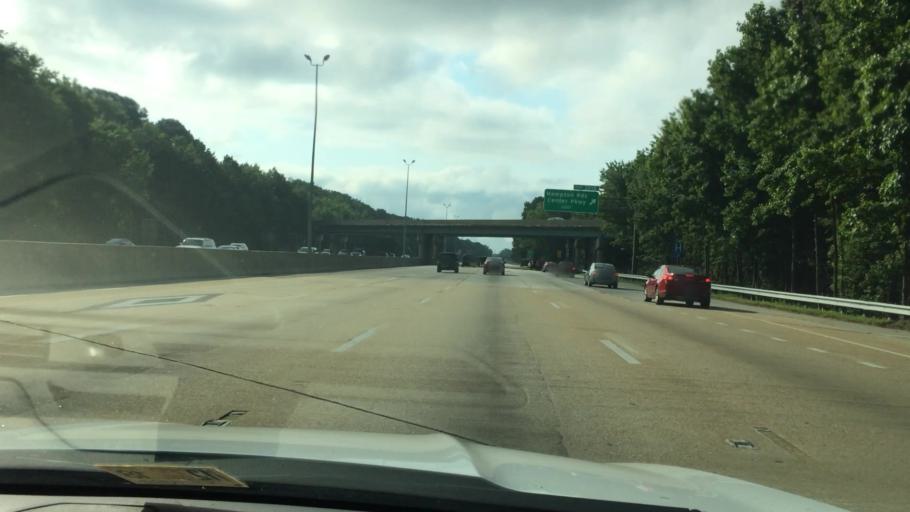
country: US
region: Virginia
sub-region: City of Hampton
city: Hampton
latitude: 37.0602
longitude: -76.4193
